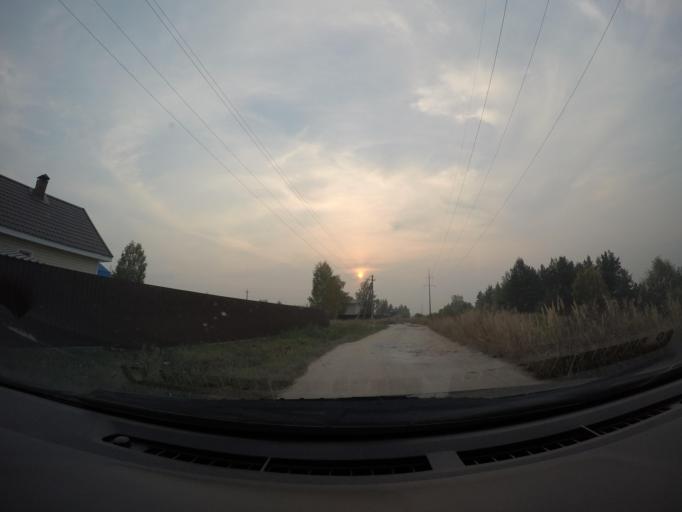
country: RU
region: Moskovskaya
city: Imeni Tsyurupy
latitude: 55.4996
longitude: 38.6626
